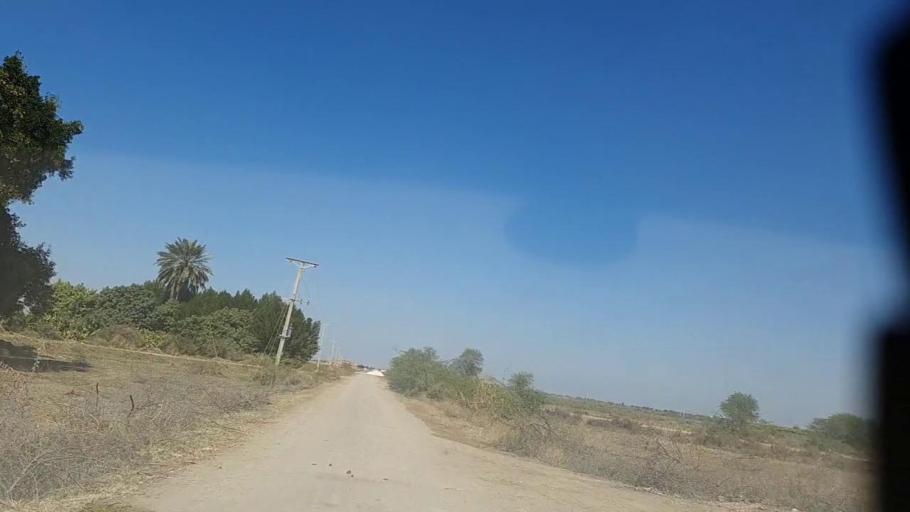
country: PK
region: Sindh
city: Digri
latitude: 25.1524
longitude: 69.0487
